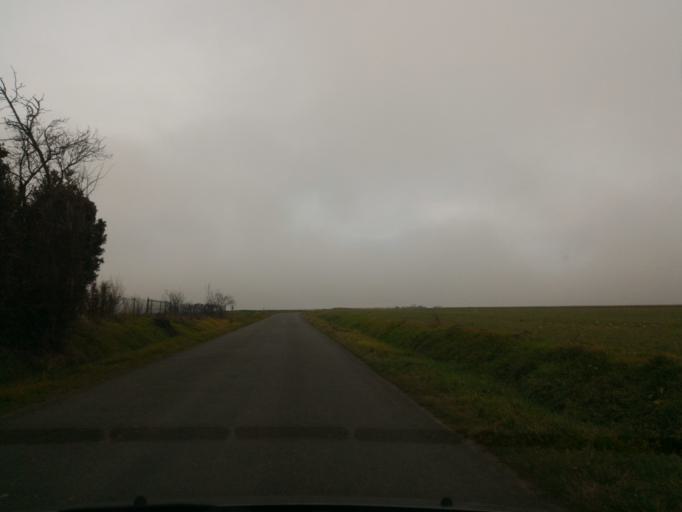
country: FR
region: Poitou-Charentes
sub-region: Departement de la Charente
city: Rouillac
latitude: 45.7468
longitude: -0.0902
